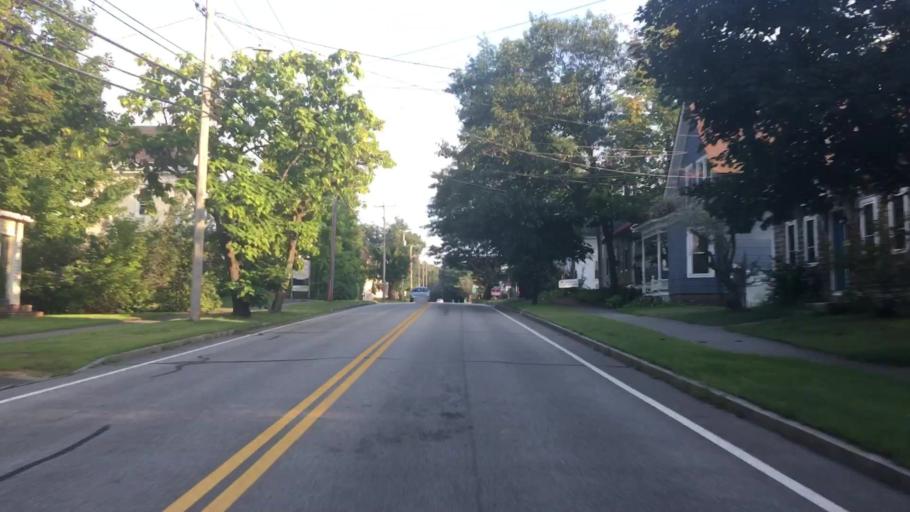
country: US
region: New Hampshire
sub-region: Belknap County
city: Laconia
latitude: 43.5207
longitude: -71.4655
